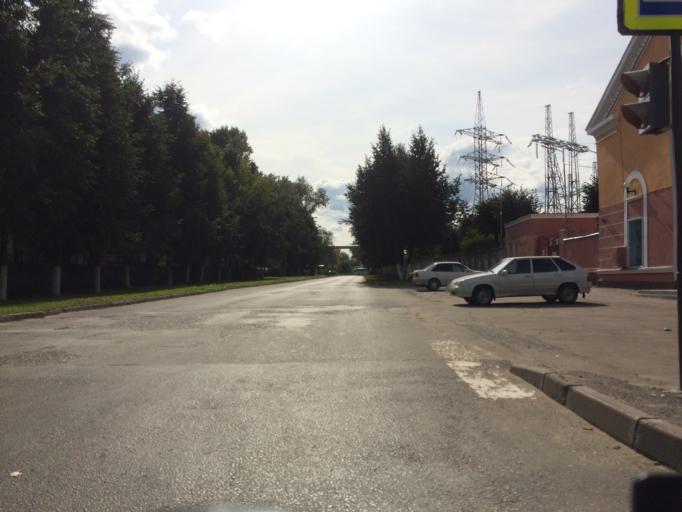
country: RU
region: Mariy-El
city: Yoshkar-Ola
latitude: 56.6317
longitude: 47.8760
